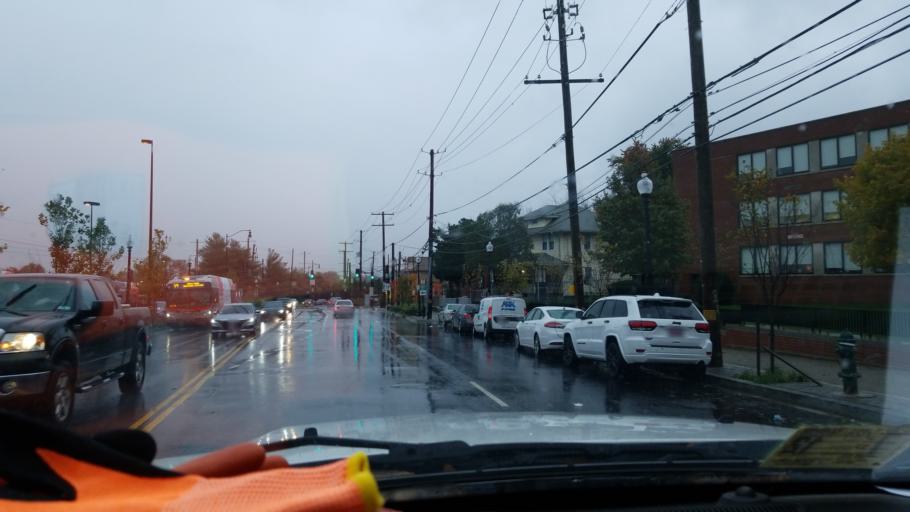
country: US
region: Maryland
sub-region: Prince George's County
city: Fairmount Heights
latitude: 38.8974
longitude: -76.9466
